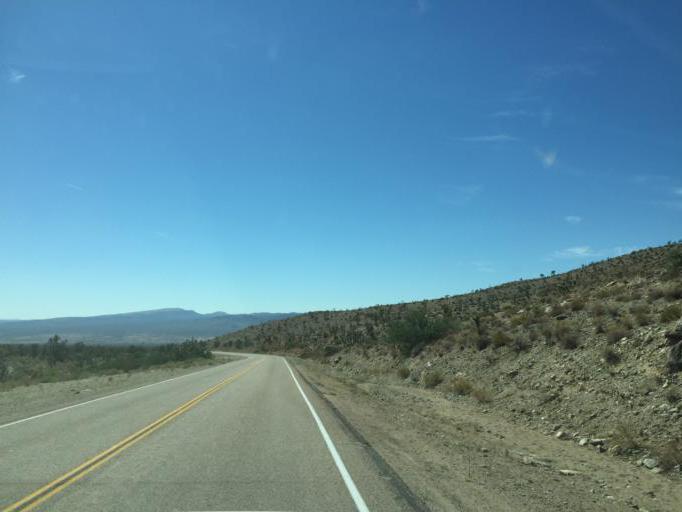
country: US
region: Arizona
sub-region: Mohave County
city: Meadview
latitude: 35.8559
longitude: -114.0790
